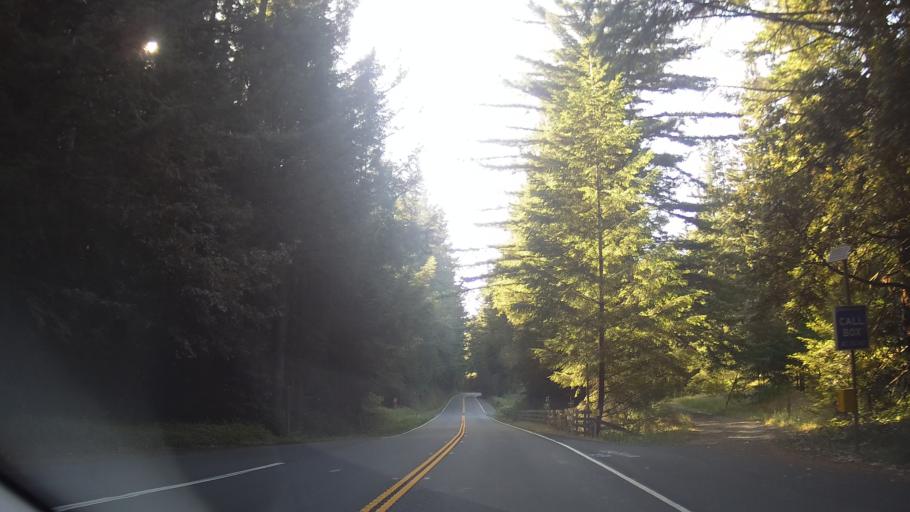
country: US
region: California
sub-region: Mendocino County
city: Fort Bragg
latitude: 39.3491
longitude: -123.6027
